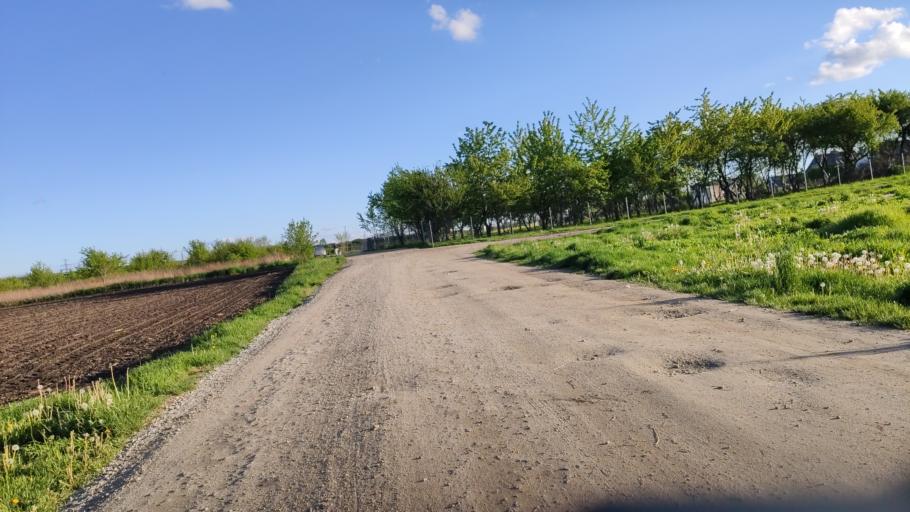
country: PL
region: Lower Silesian Voivodeship
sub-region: Powiat wroclawski
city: Zerniki Wroclawskie
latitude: 51.0453
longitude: 17.0653
